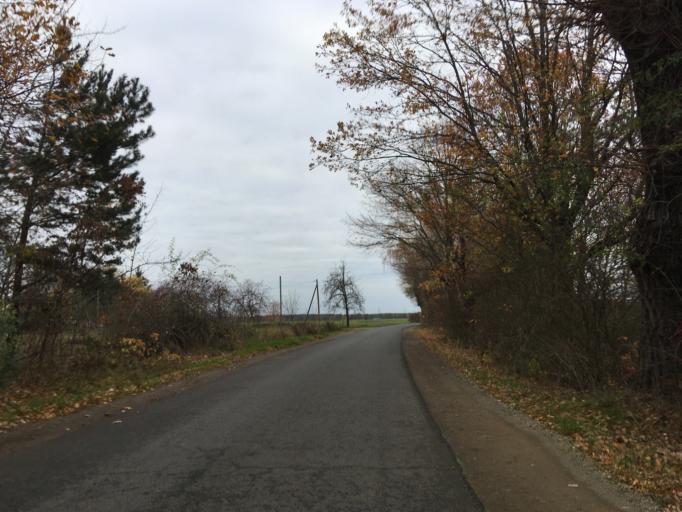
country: DE
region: Brandenburg
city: Drehnow
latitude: 51.8512
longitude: 14.3345
